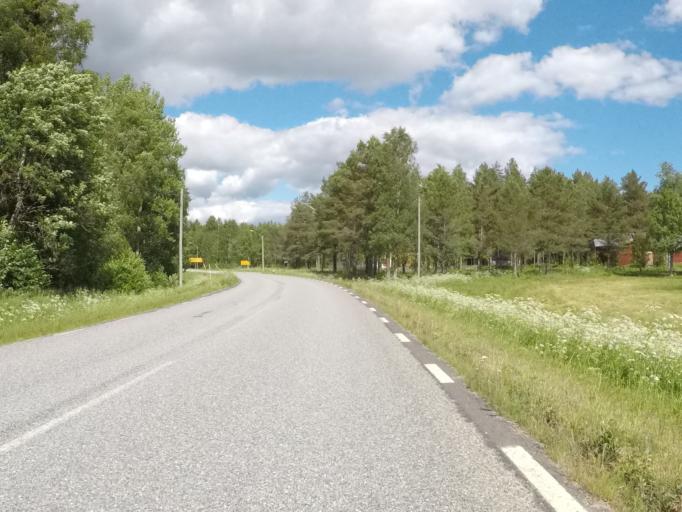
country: SE
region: Vaesterbotten
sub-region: Robertsfors Kommun
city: Robertsfors
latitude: 63.9662
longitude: 20.8119
